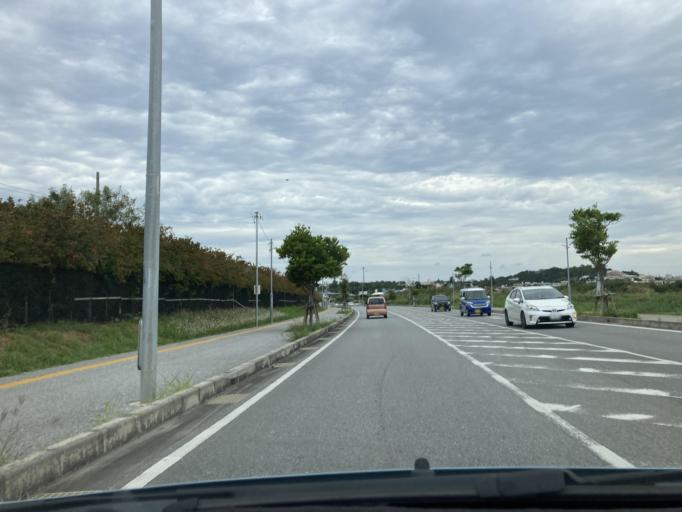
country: JP
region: Okinawa
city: Ishikawa
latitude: 26.3968
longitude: 127.7408
